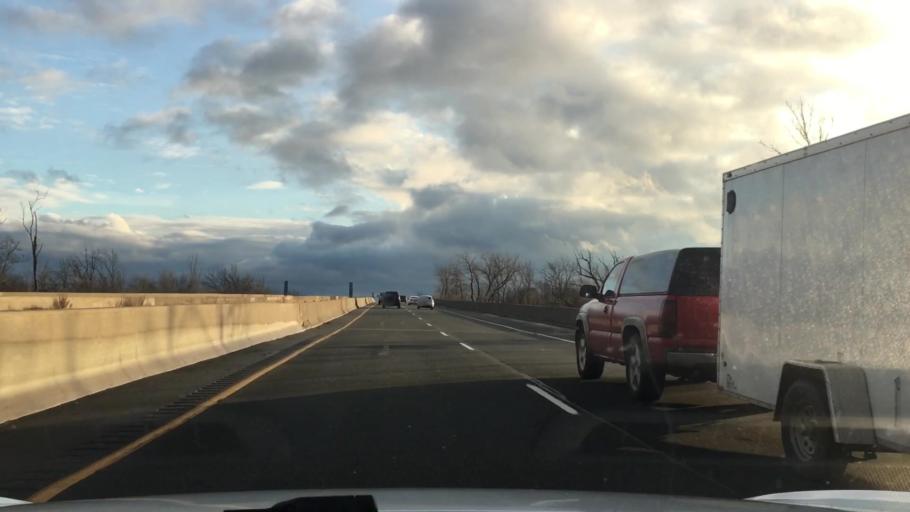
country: CA
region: Ontario
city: Niagara Falls
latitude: 43.0472
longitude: -79.1218
